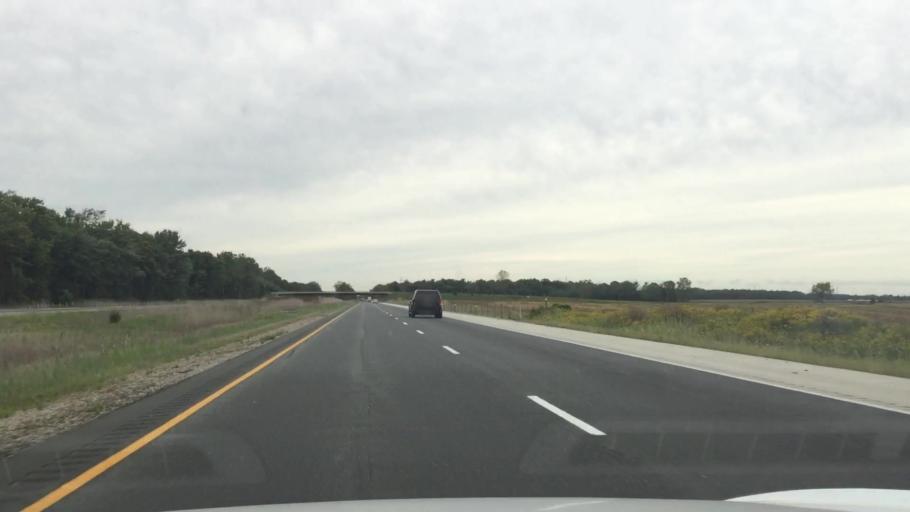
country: CA
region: Ontario
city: Camlachie
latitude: 42.9914
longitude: -82.0416
